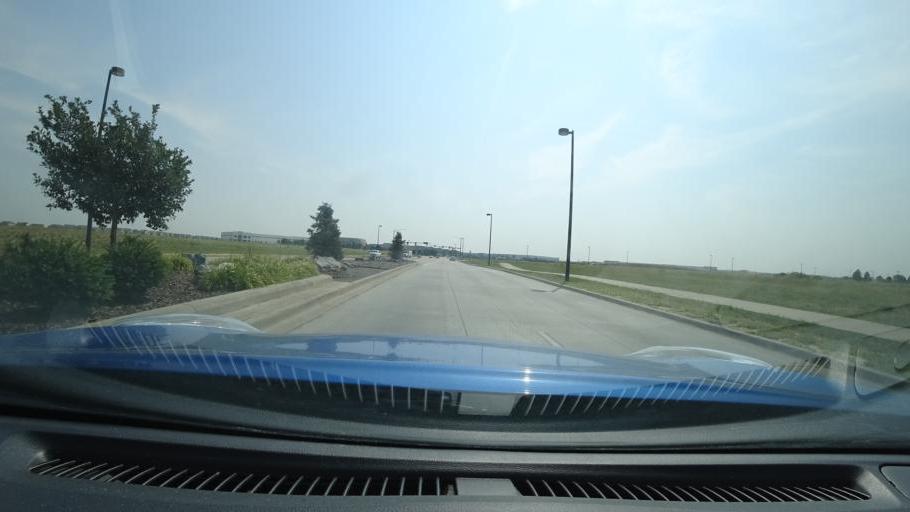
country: US
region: Colorado
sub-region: Adams County
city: Aurora
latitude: 39.7728
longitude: -104.7859
